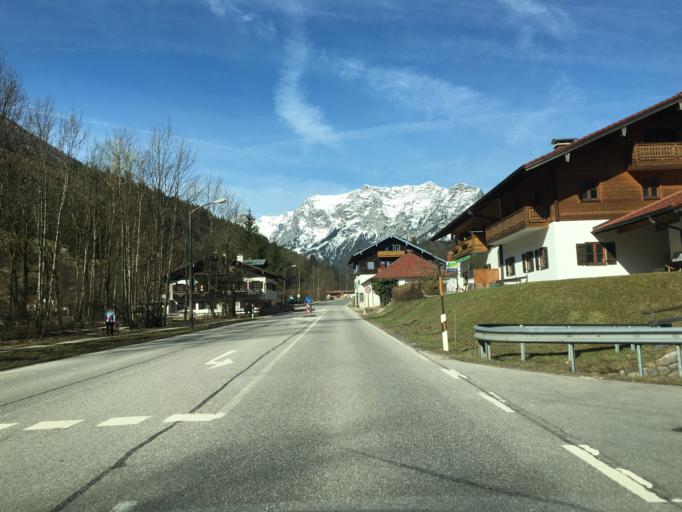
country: DE
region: Bavaria
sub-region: Upper Bavaria
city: Ramsau
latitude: 47.6047
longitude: 12.9166
